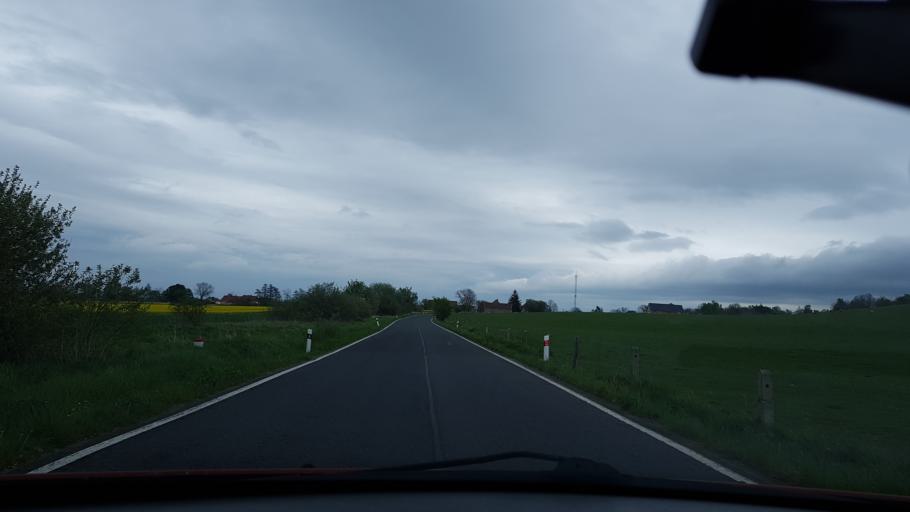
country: PL
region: Opole Voivodeship
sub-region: Powiat nyski
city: Kamienica
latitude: 50.4273
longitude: 16.9599
